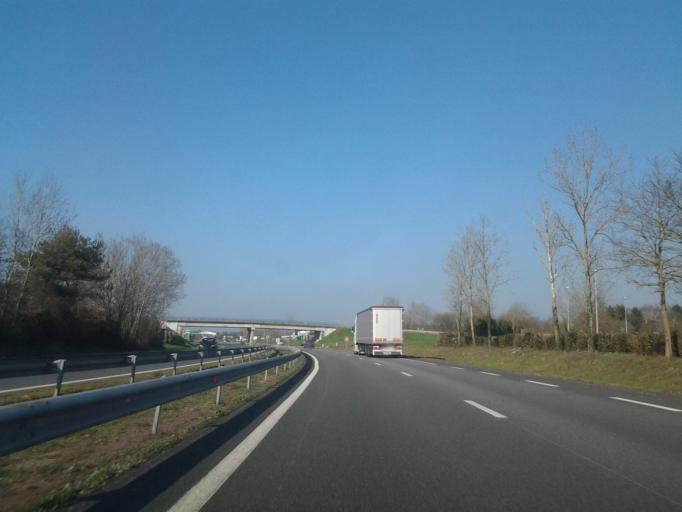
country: FR
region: Pays de la Loire
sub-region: Departement de la Vendee
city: La Genetouze
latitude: 46.7240
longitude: -1.5576
